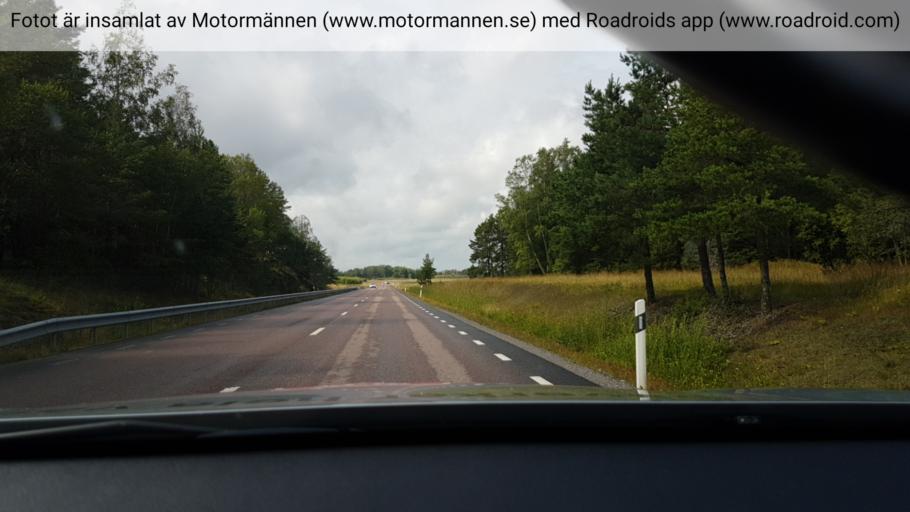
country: SE
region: Uppsala
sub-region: Osthammars Kommun
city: Bjorklinge
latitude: 59.9335
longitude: 17.4784
